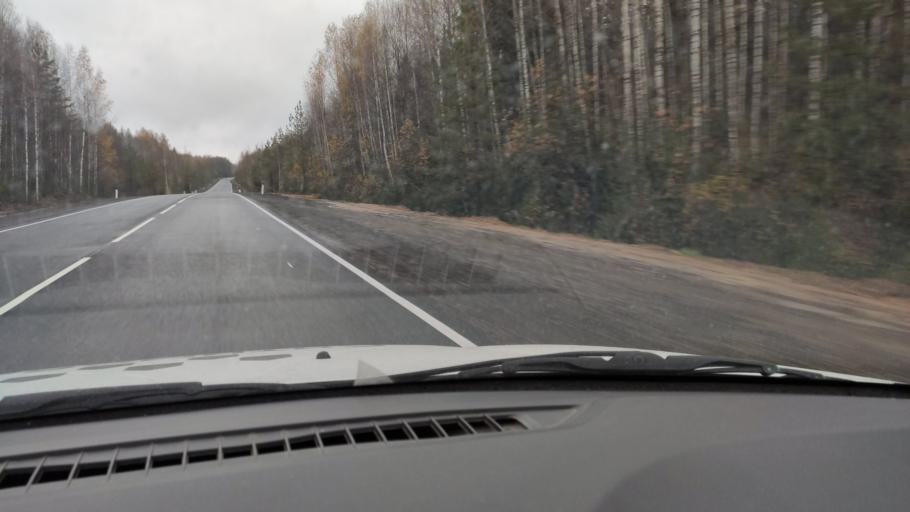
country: RU
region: Kirov
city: Chernaya Kholunitsa
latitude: 58.8766
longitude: 51.4771
